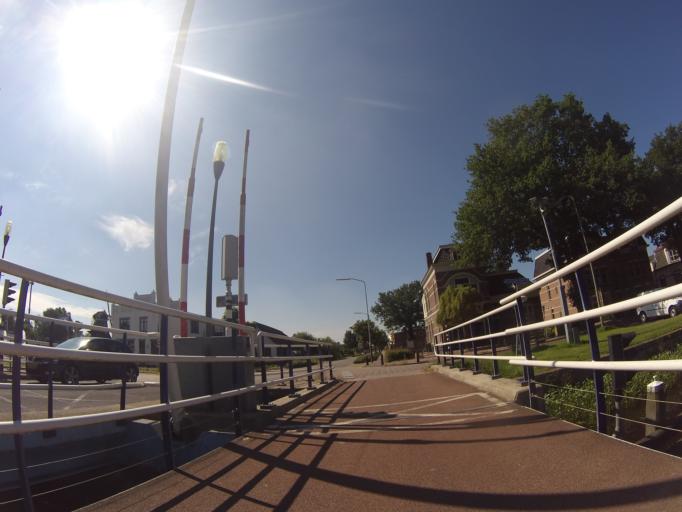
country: NL
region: Drenthe
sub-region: Gemeente Emmen
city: Schoonebeek
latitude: 52.7098
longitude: 6.9253
